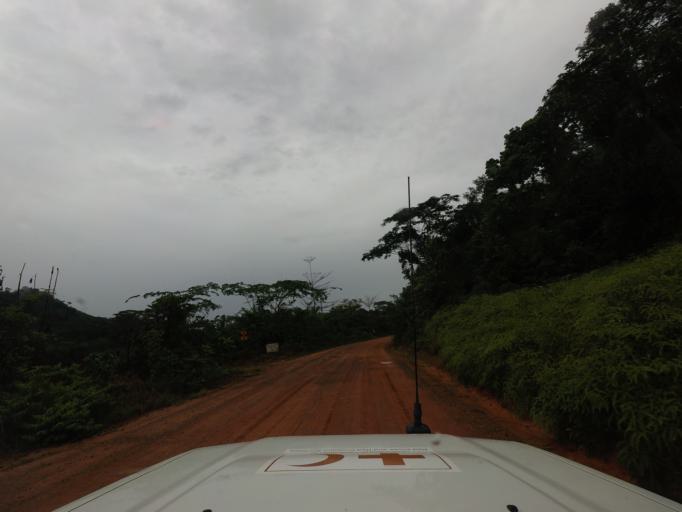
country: LR
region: Nimba
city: Sanniquellie
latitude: 7.4181
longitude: -8.6497
